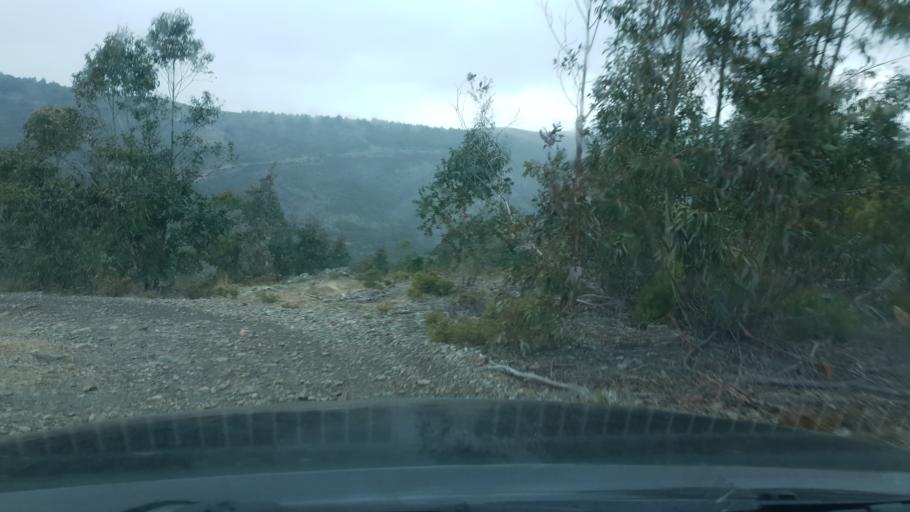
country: PT
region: Viseu
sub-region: Sao Pedro do Sul
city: Sao Pedro do Sul
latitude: 40.8587
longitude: -8.0979
